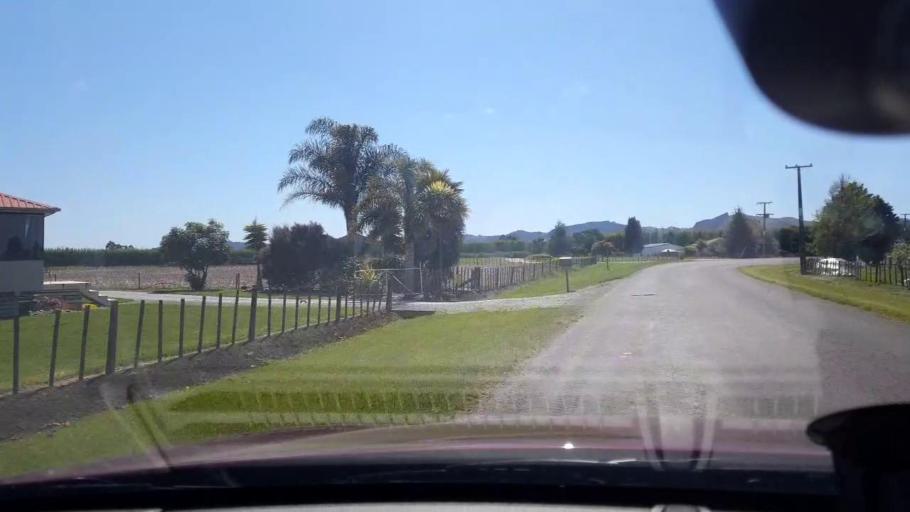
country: NZ
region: Gisborne
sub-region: Gisborne District
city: Gisborne
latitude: -38.6372
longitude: 177.9406
